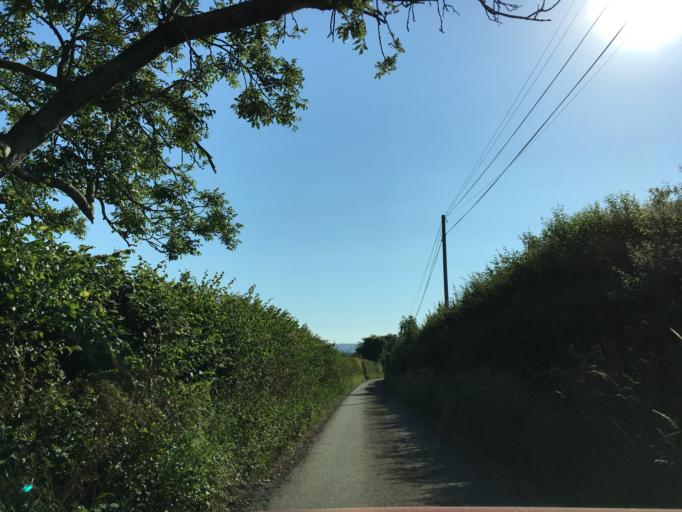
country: GB
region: England
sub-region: South Gloucestershire
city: Pucklechurch
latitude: 51.4709
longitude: -2.4309
